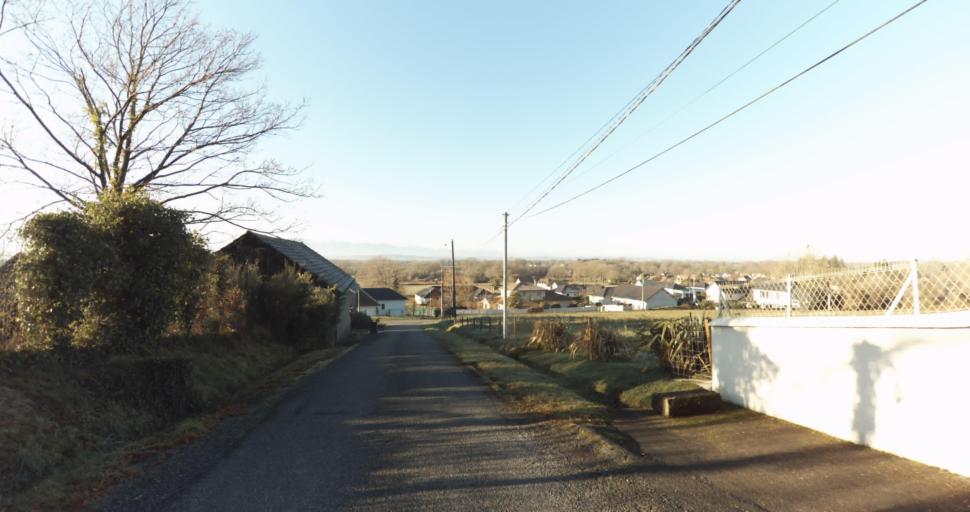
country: FR
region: Aquitaine
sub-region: Departement des Pyrenees-Atlantiques
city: Morlaas
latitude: 43.3291
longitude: -0.2773
